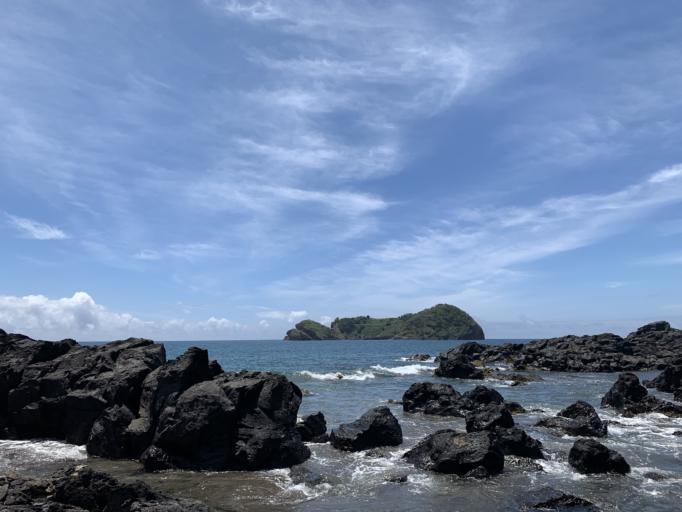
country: PT
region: Azores
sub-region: Vila Franca do Campo
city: Vila Franca do Campo
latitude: 37.7139
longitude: -25.4380
